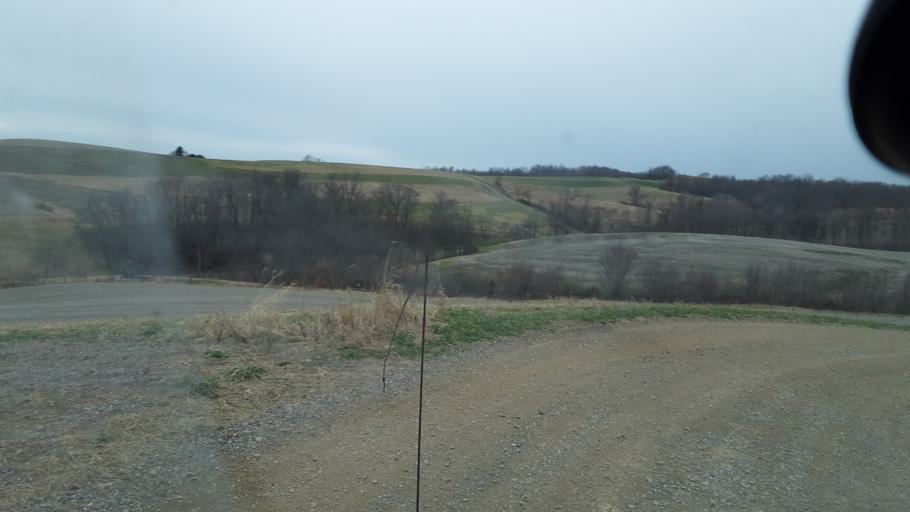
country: US
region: Ohio
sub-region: Coshocton County
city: West Lafayette
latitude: 40.3385
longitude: -81.6981
